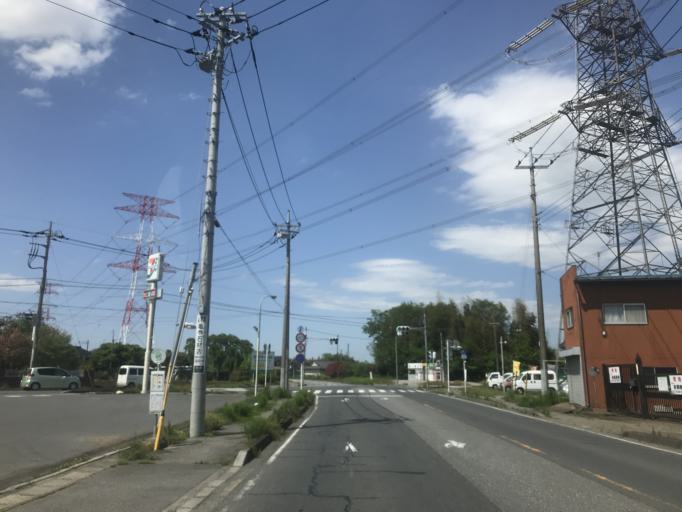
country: JP
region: Chiba
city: Noda
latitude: 35.9546
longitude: 139.9102
